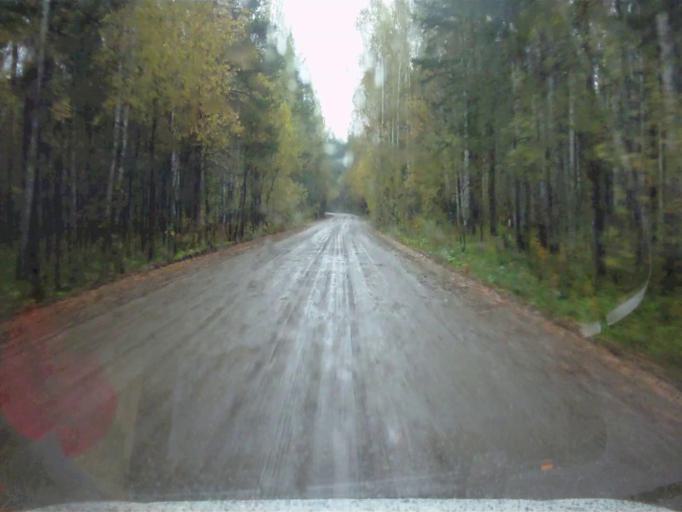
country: RU
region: Chelyabinsk
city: Kyshtym
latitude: 55.8902
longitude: 60.4651
